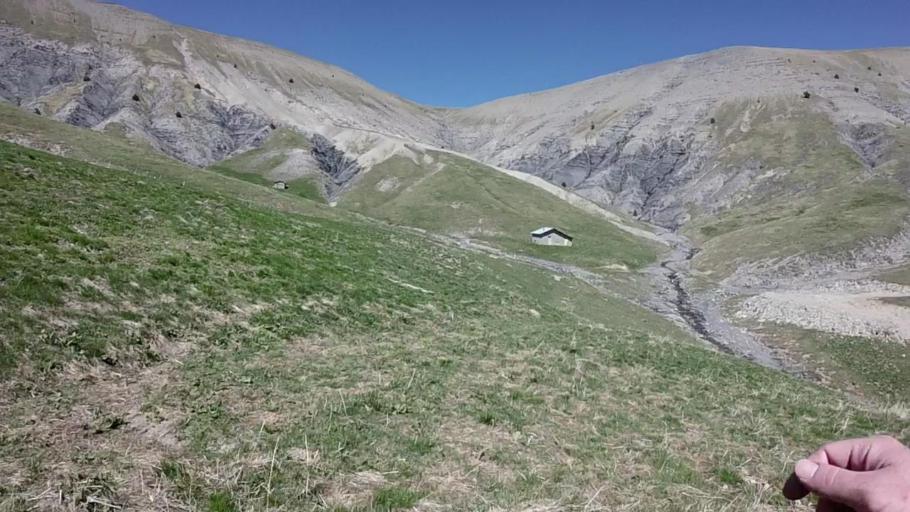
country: FR
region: Provence-Alpes-Cote d'Azur
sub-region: Departement des Alpes-de-Haute-Provence
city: Seyne-les-Alpes
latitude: 44.3294
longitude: 6.2831
